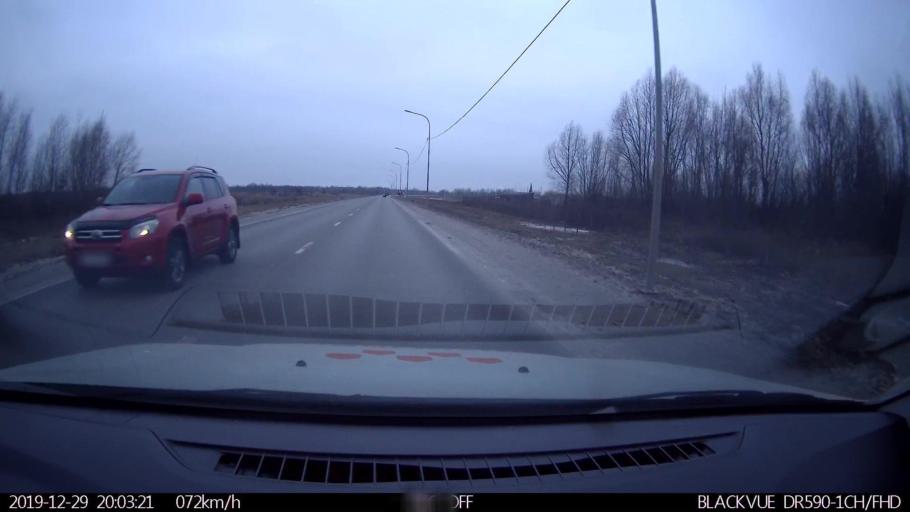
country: RU
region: Nizjnij Novgorod
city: Nizhniy Novgorod
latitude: 56.3734
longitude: 44.0193
